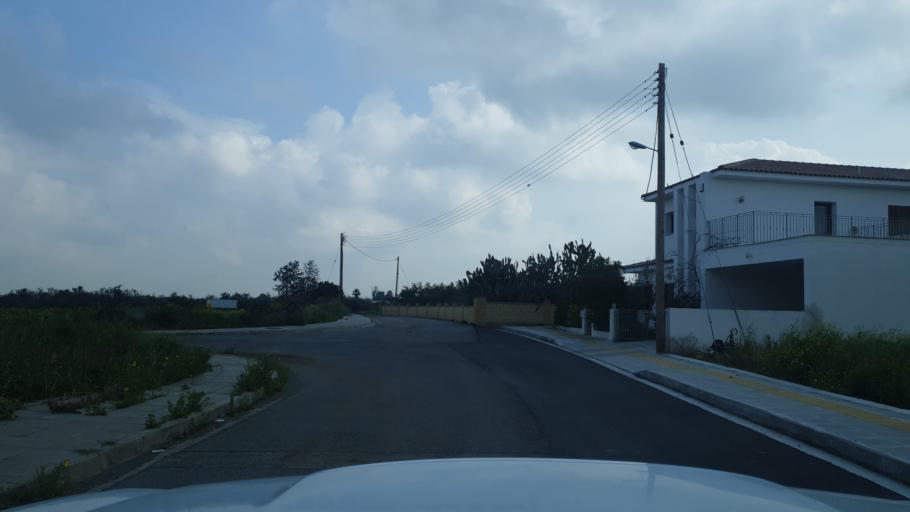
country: CY
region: Lefkosia
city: Kato Deftera
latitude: 35.0855
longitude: 33.2899
